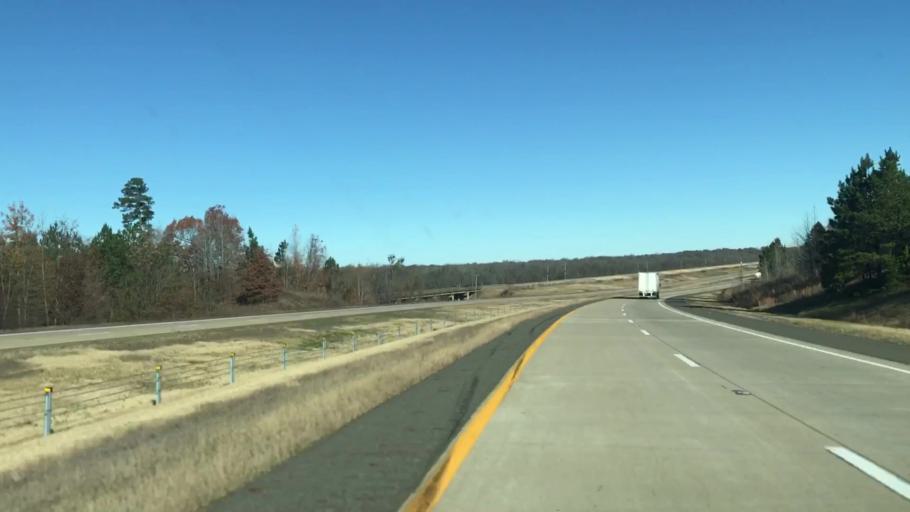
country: US
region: Texas
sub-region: Cass County
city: Queen City
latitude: 33.1336
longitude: -93.8945
